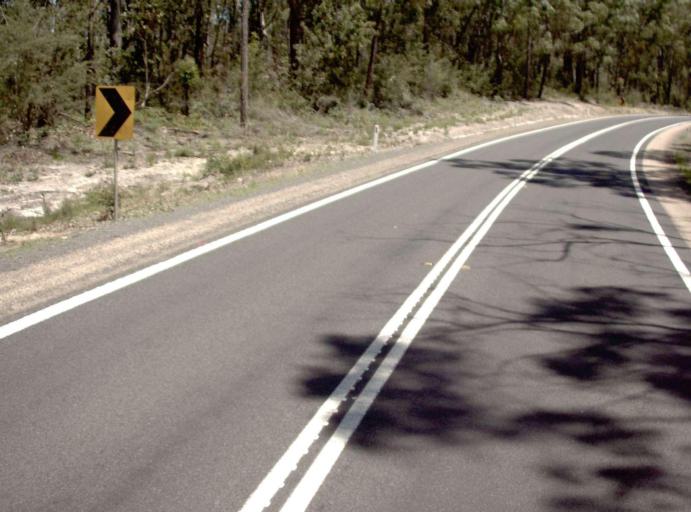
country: AU
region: Victoria
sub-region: East Gippsland
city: Lakes Entrance
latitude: -37.6930
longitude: 148.7490
